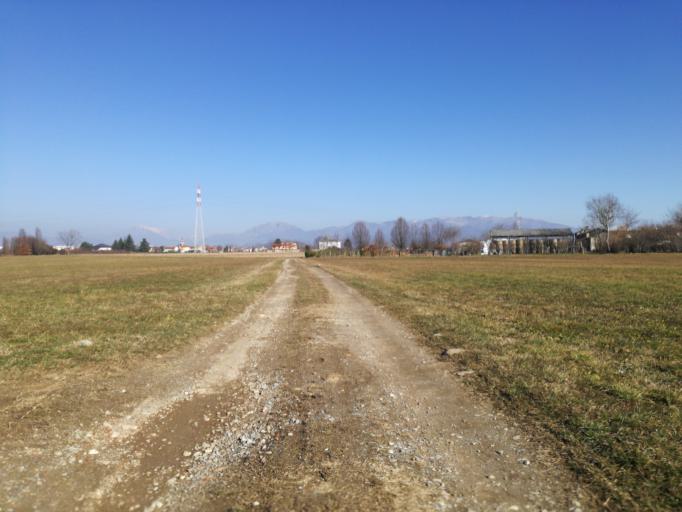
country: IT
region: Lombardy
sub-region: Provincia di Lecco
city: Verderio Superiore
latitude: 45.6542
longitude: 9.4409
